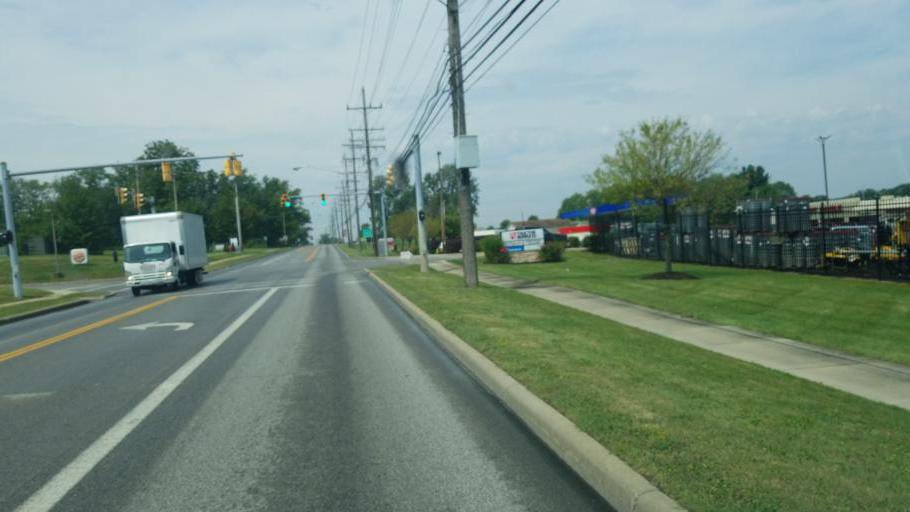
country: US
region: Ohio
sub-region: Geauga County
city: Middlefield
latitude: 41.4633
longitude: -81.0908
